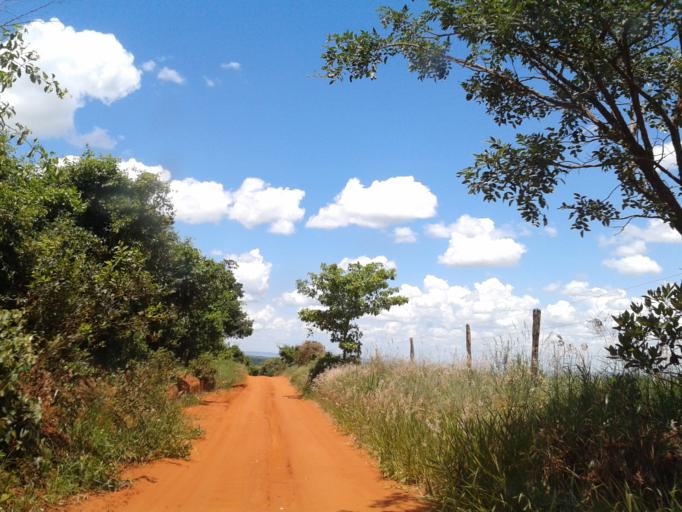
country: BR
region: Minas Gerais
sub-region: Centralina
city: Centralina
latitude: -18.6988
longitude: -49.1532
